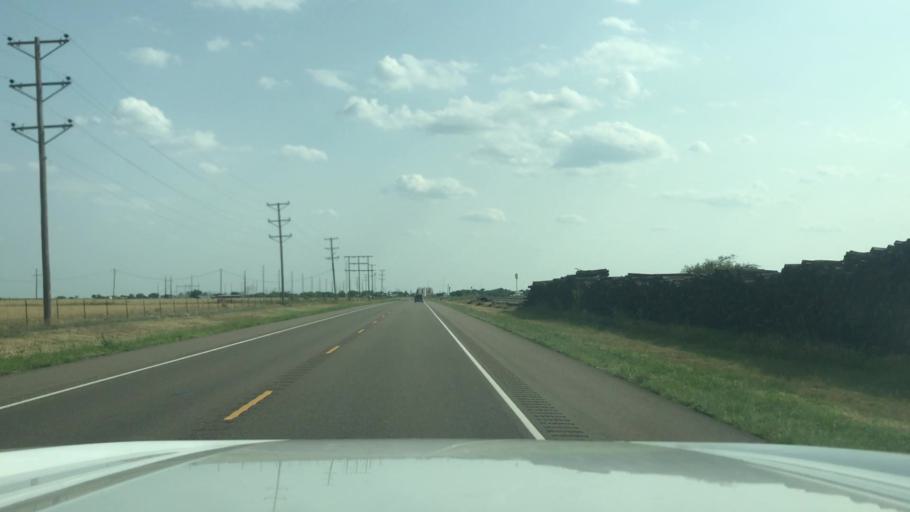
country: US
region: Texas
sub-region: Hartley County
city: Channing
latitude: 35.6999
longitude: -102.3267
